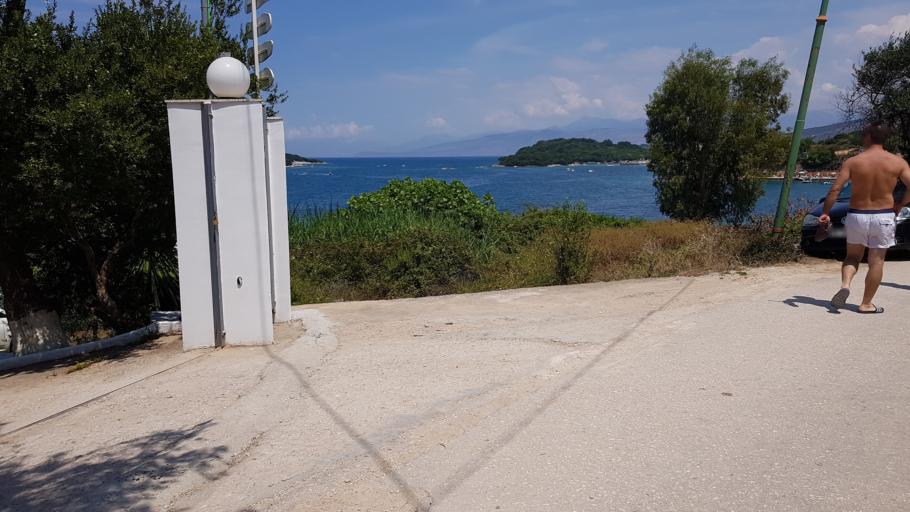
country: AL
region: Vlore
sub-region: Rrethi i Sarandes
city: Xarre
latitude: 39.7668
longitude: 19.9973
